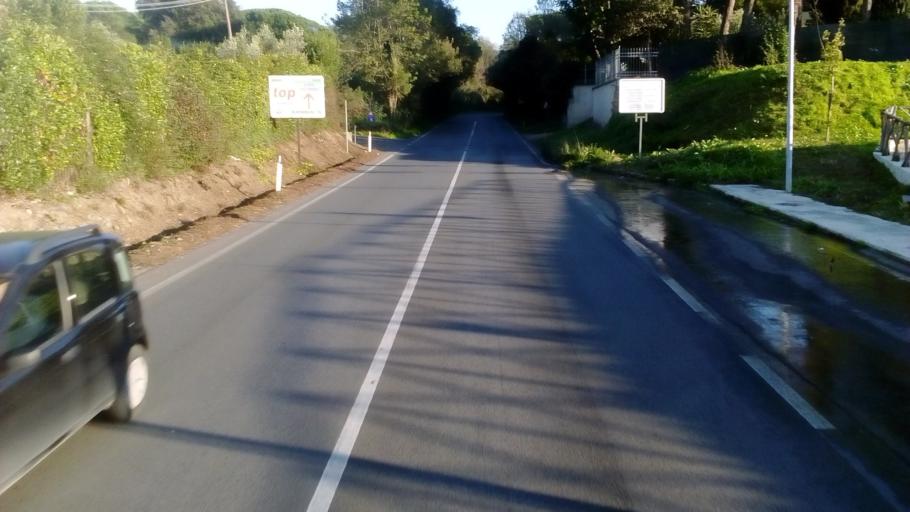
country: IT
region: Latium
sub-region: Citta metropolitana di Roma Capitale
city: Albano Laziale
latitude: 41.7173
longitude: 12.6263
